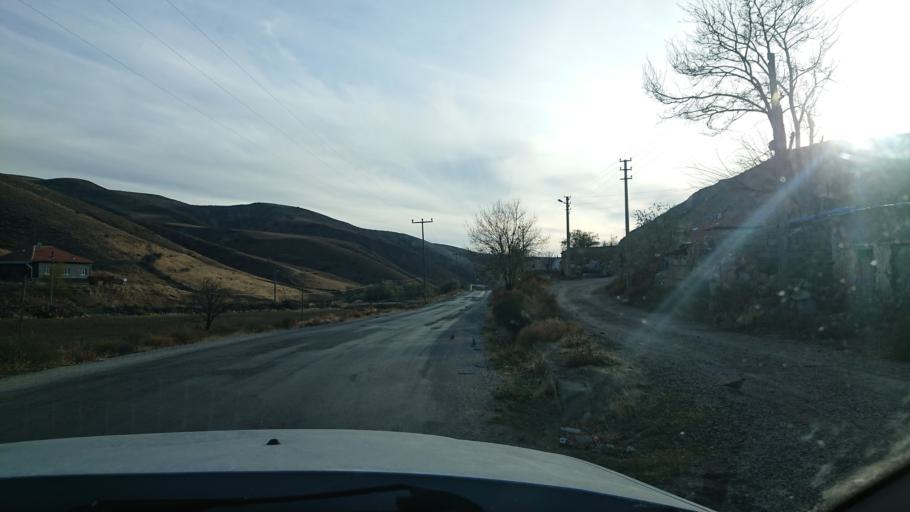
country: TR
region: Ankara
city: Sereflikochisar
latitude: 38.7634
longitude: 33.6985
